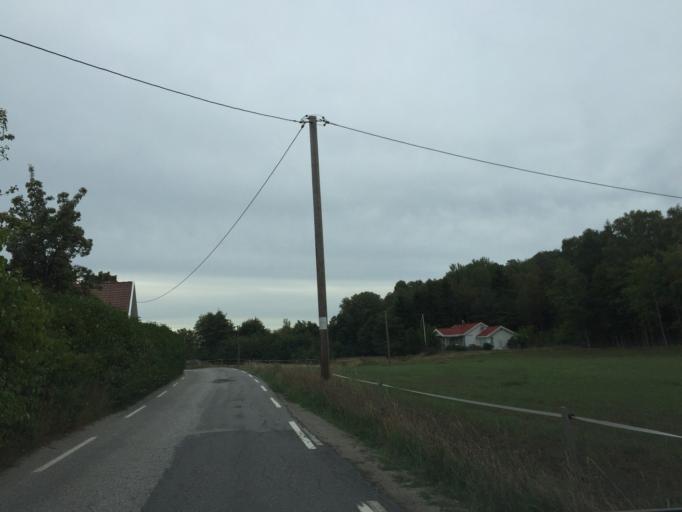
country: NO
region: Ostfold
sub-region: Hvaler
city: Skjaerhalden
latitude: 59.0573
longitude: 11.0362
